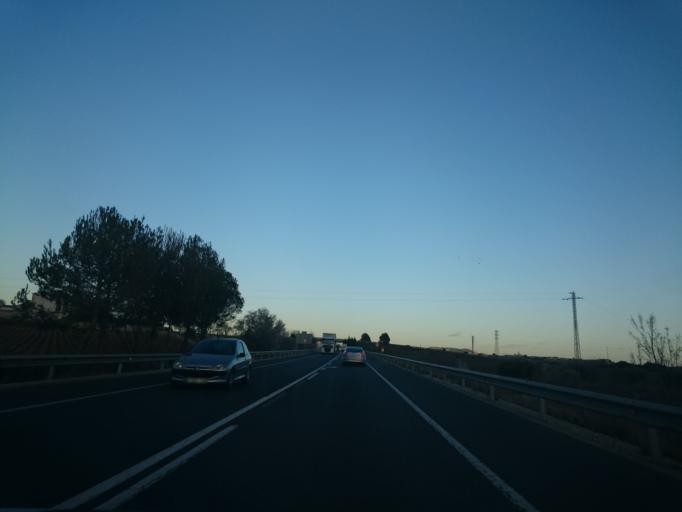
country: ES
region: Catalonia
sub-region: Provincia de Barcelona
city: Vilafranca del Penedes
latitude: 41.3325
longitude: 1.6603
